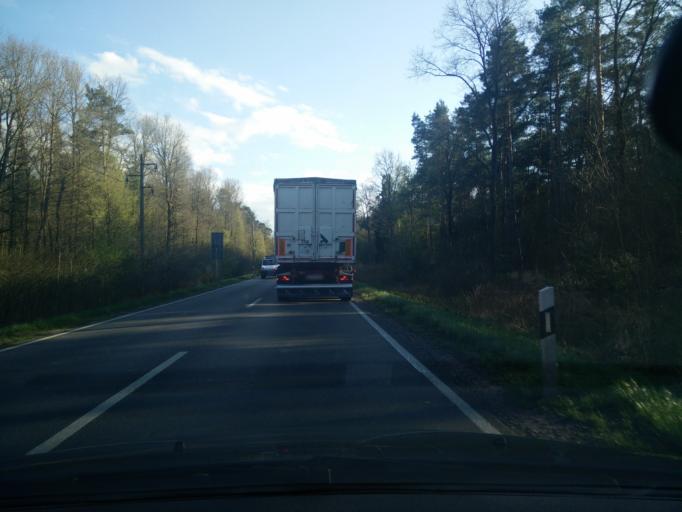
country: DE
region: Rheinland-Pfalz
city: Kandel
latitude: 49.0607
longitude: 8.2031
